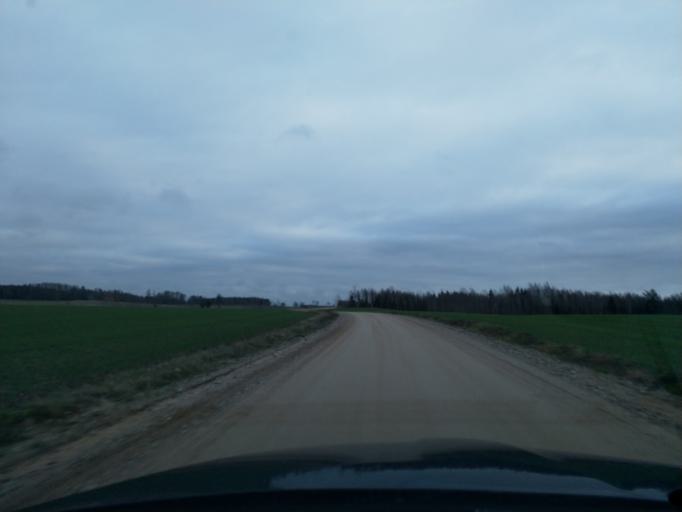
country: LV
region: Kuldigas Rajons
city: Kuldiga
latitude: 56.8937
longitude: 22.2637
